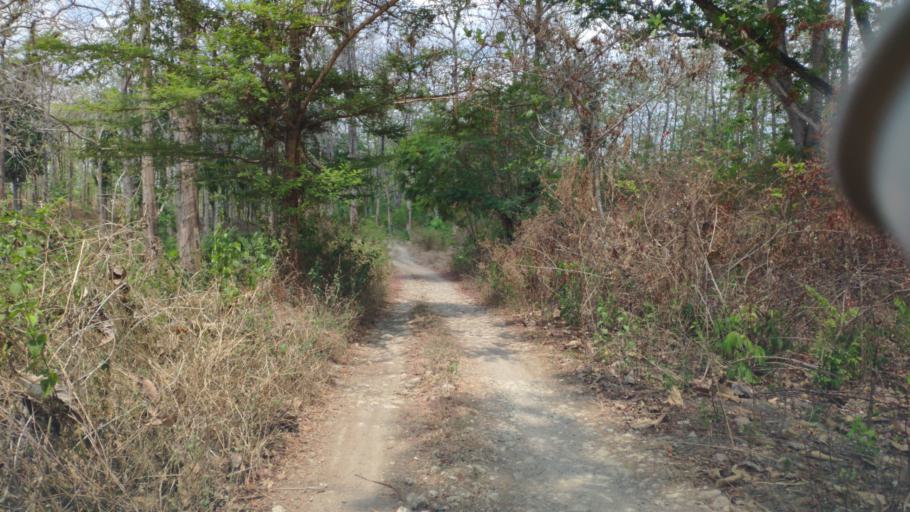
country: ID
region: Central Java
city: Singonegoro
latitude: -6.9942
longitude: 111.5301
